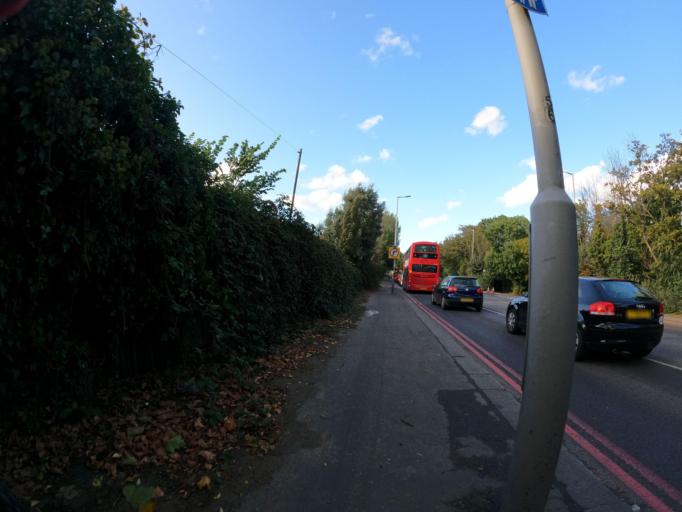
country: GB
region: England
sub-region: Greater London
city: Ealing Broadway
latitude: 51.5206
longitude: -0.2916
